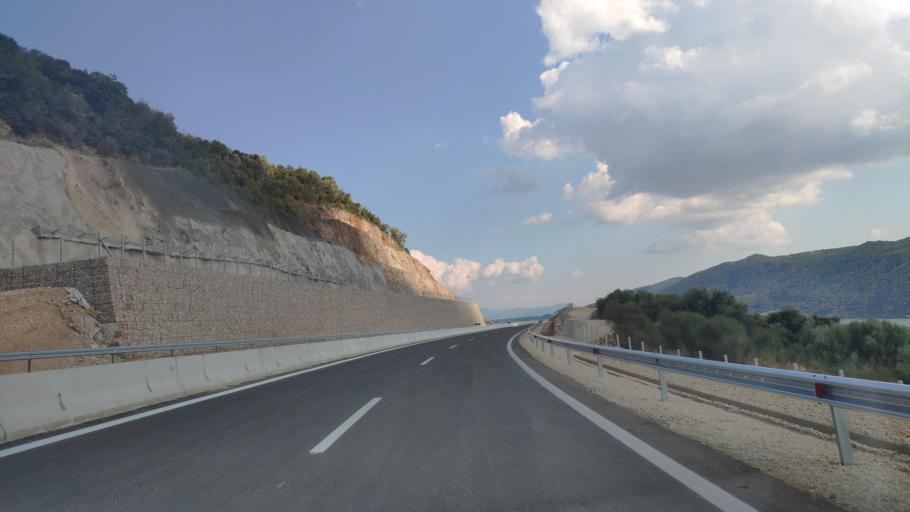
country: GR
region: West Greece
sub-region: Nomos Aitolias kai Akarnanias
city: Stanos
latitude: 38.7759
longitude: 21.1555
